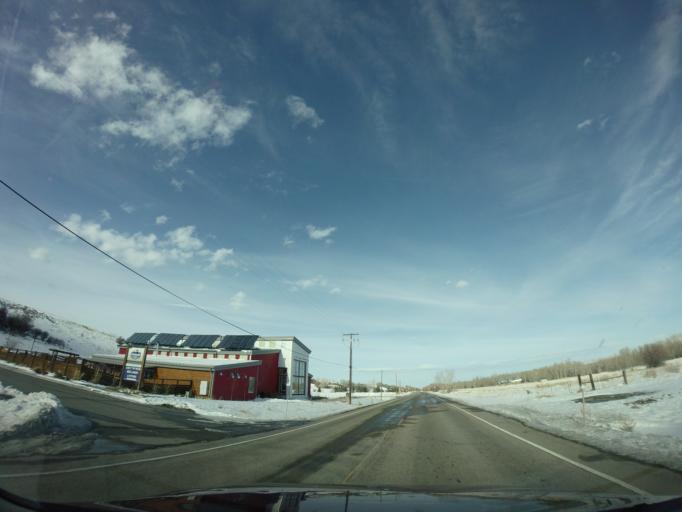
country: US
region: Montana
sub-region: Carbon County
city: Red Lodge
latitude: 45.2016
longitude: -109.2454
